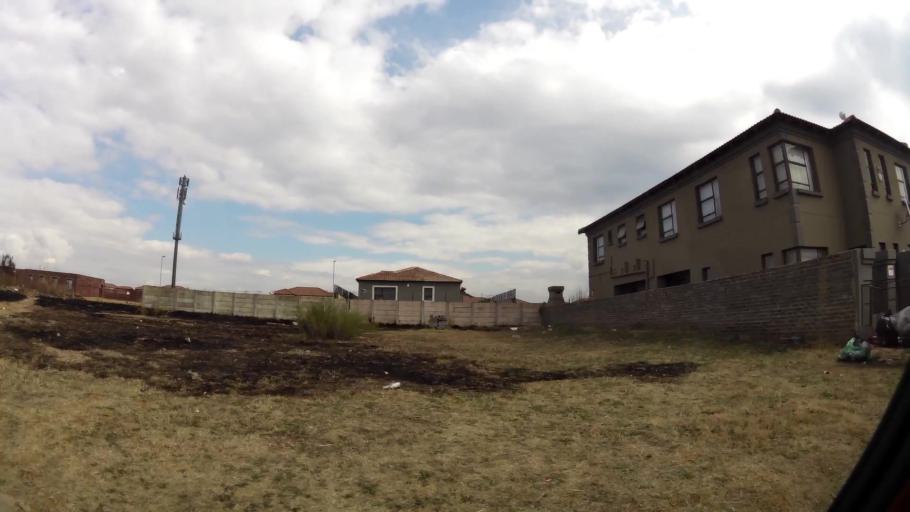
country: ZA
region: Gauteng
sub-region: Sedibeng District Municipality
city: Vanderbijlpark
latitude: -26.7154
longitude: 27.8842
